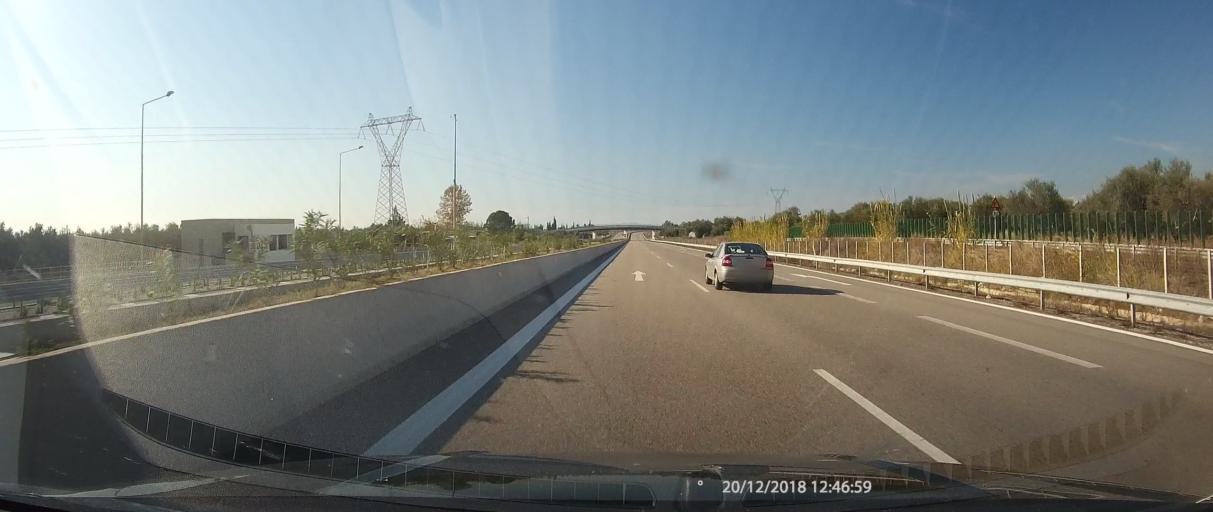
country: GR
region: West Greece
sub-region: Nomos Aitolias kai Akarnanias
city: Mesolongi
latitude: 38.3921
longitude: 21.4590
